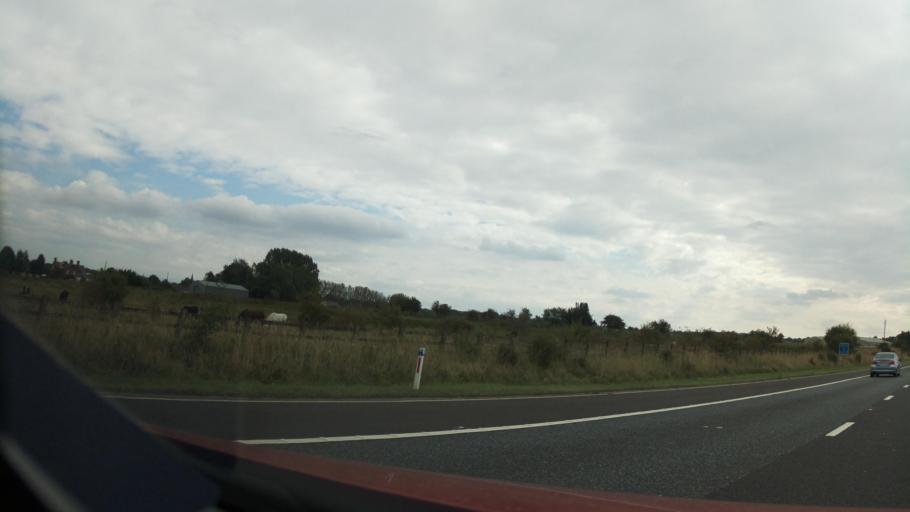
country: GB
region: England
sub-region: County Durham
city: West Rainton
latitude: 54.8226
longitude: -1.5229
